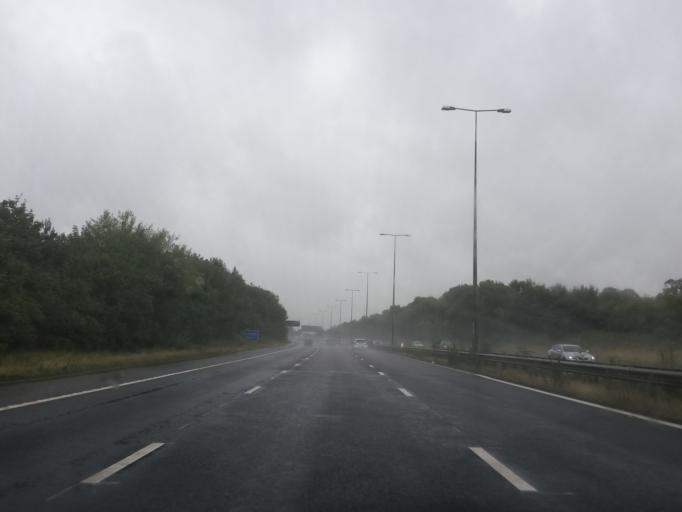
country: GB
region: England
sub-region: Leicestershire
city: Kegworth
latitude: 52.8085
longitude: -1.3053
